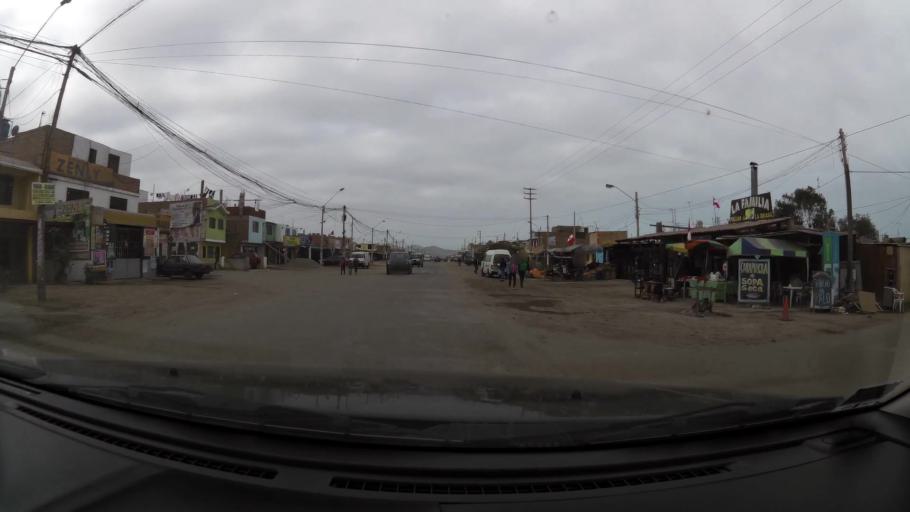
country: PE
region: Lima
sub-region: Provincia de Canete
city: Chilca
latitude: -12.5148
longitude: -76.7350
